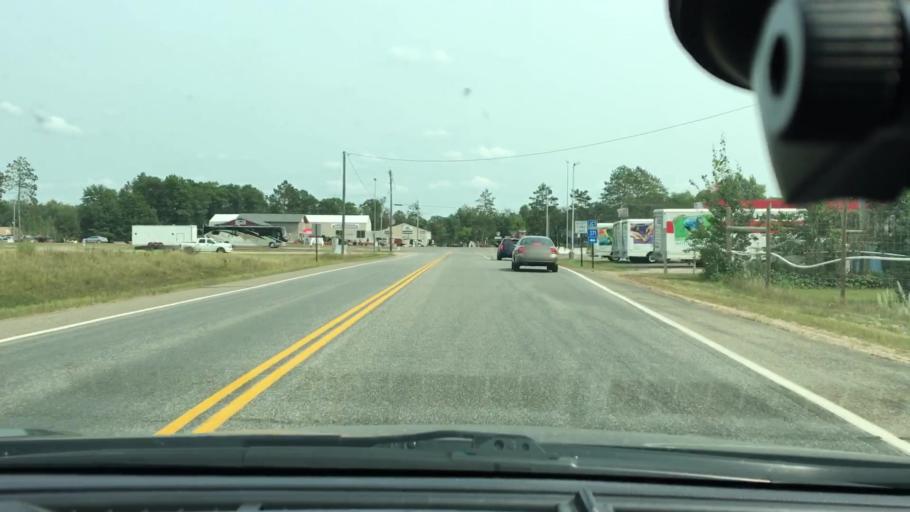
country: US
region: Minnesota
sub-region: Cass County
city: East Gull Lake
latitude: 46.4127
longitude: -94.2877
